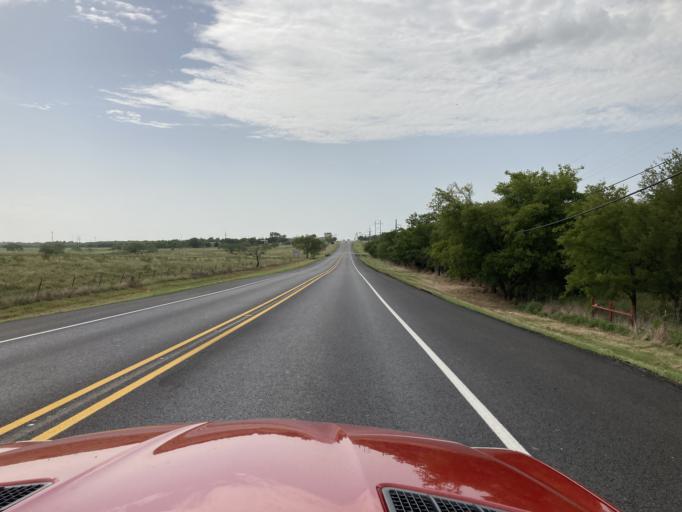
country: US
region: Texas
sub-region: Navarro County
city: Corsicana
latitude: 32.0579
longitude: -96.4298
